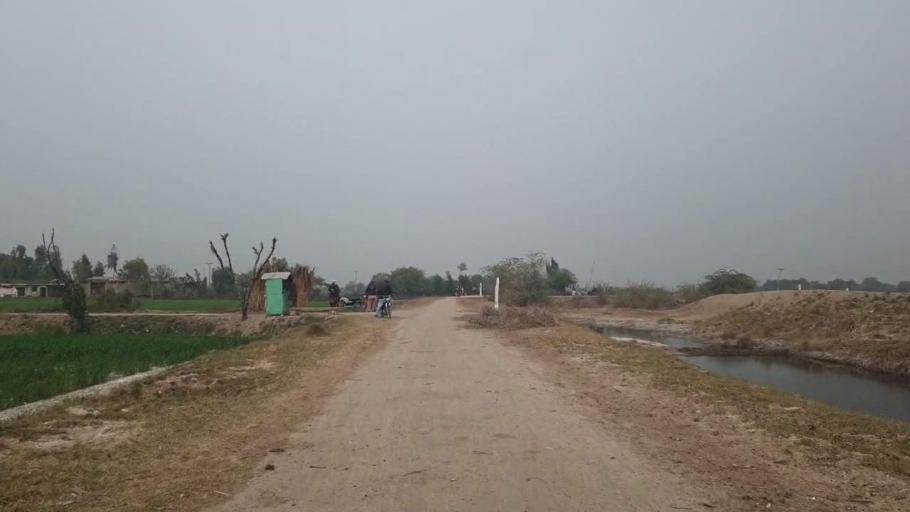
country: PK
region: Sindh
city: Tando Adam
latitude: 25.8489
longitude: 68.6641
